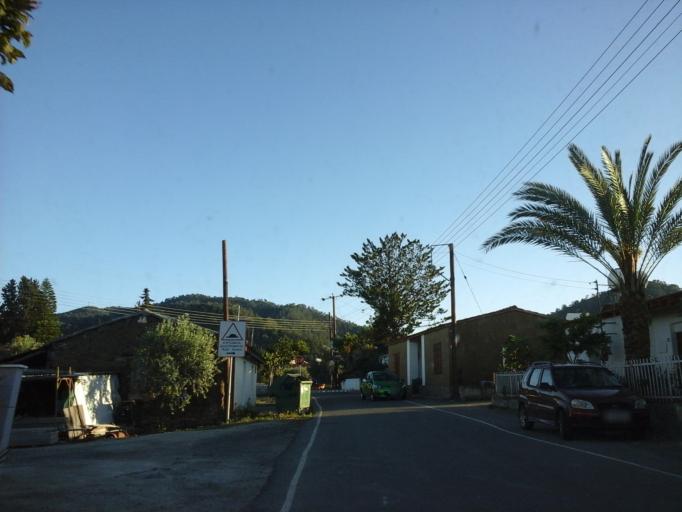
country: CY
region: Lefkosia
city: Astromeritis
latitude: 35.0700
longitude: 32.9920
